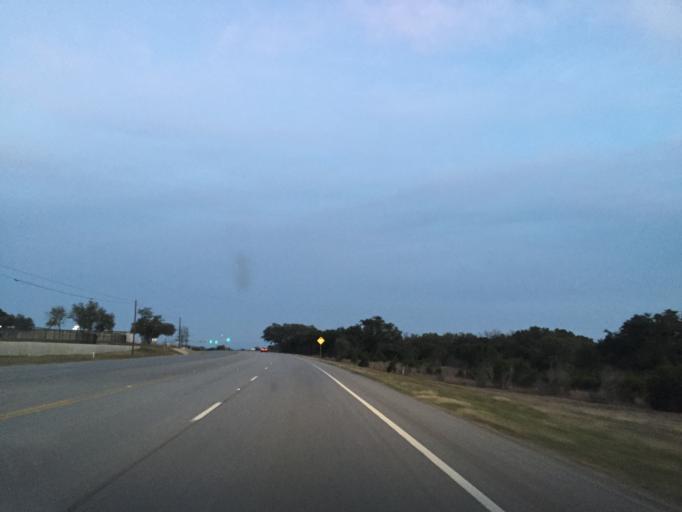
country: US
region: Texas
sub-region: Burnet County
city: Bertram
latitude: 30.6821
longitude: -97.9583
